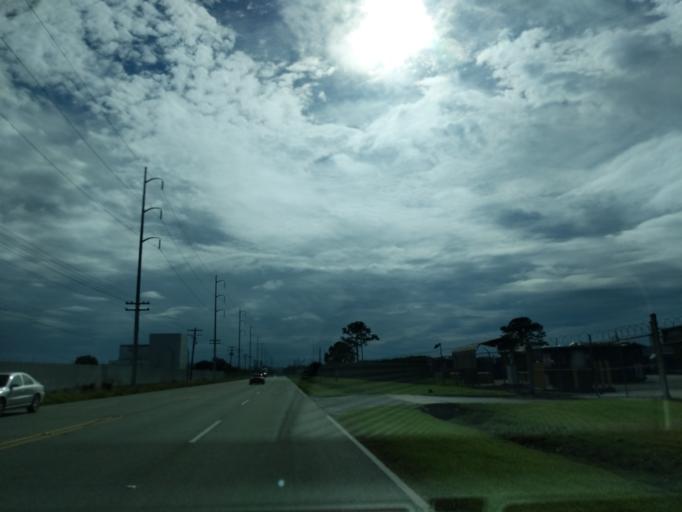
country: US
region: Louisiana
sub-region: Saint Bernard Parish
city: Chalmette
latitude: 30.0335
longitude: -89.9103
